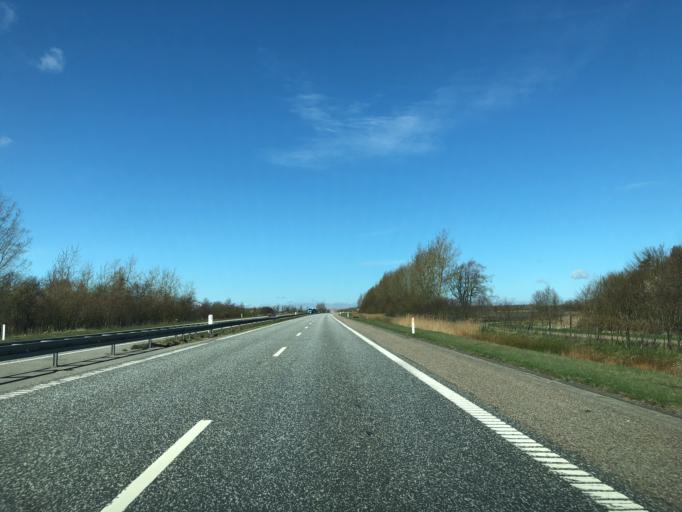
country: DK
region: North Denmark
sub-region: Alborg Kommune
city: Vestbjerg
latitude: 57.1133
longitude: 9.9503
